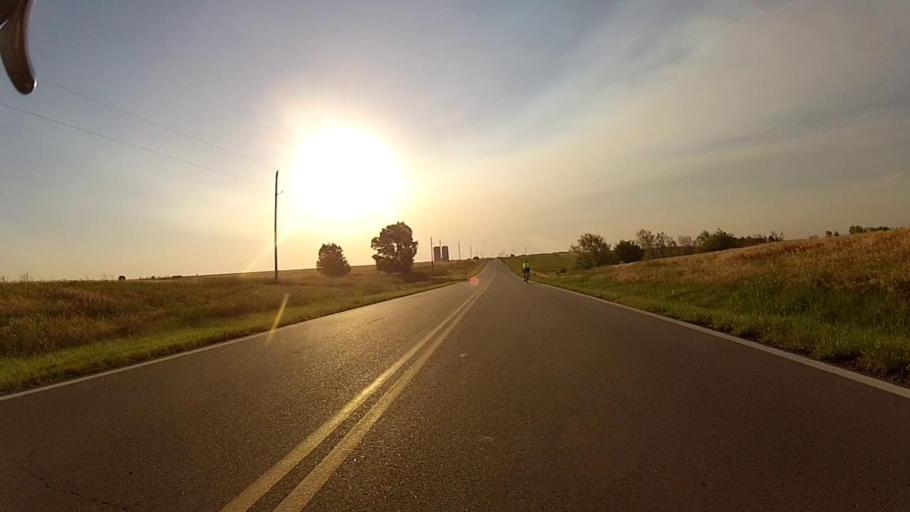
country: US
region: Kansas
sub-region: Harper County
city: Anthony
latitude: 37.1534
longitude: -97.8803
